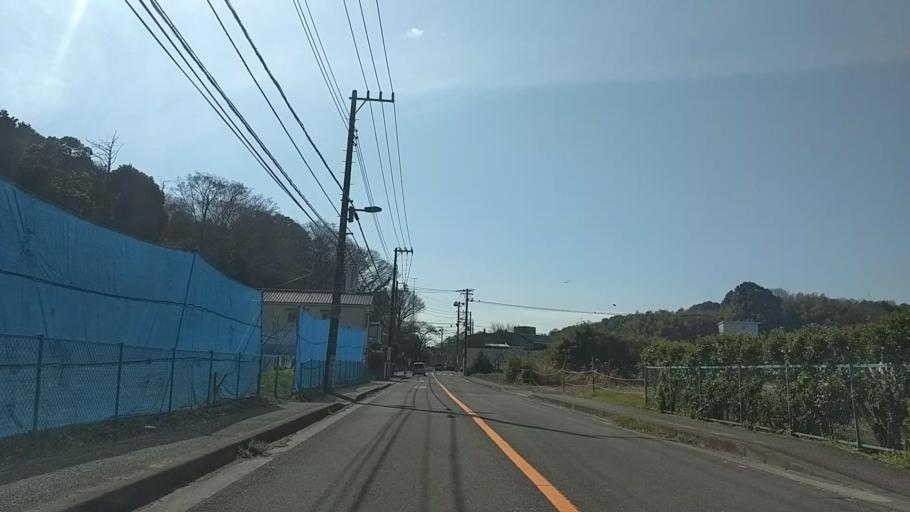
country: JP
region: Kanagawa
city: Kamakura
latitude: 35.4050
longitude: 139.5532
